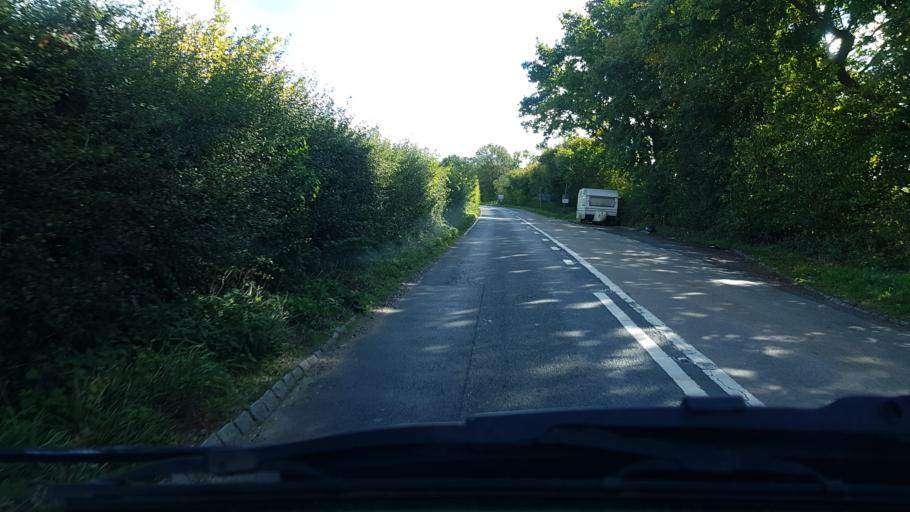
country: GB
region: England
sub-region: West Sussex
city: Billingshurst
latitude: 50.9978
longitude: -0.4677
